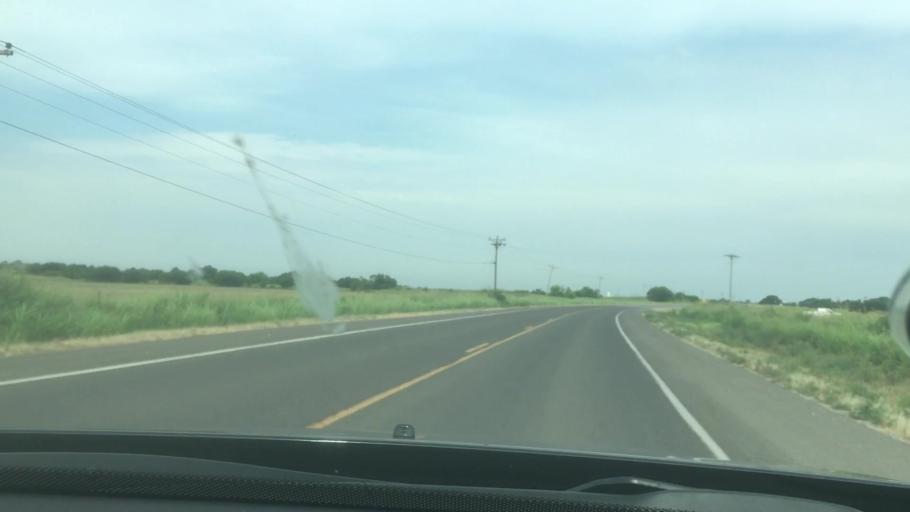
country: US
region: Oklahoma
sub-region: Garvin County
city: Maysville
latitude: 34.8193
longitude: -97.4871
